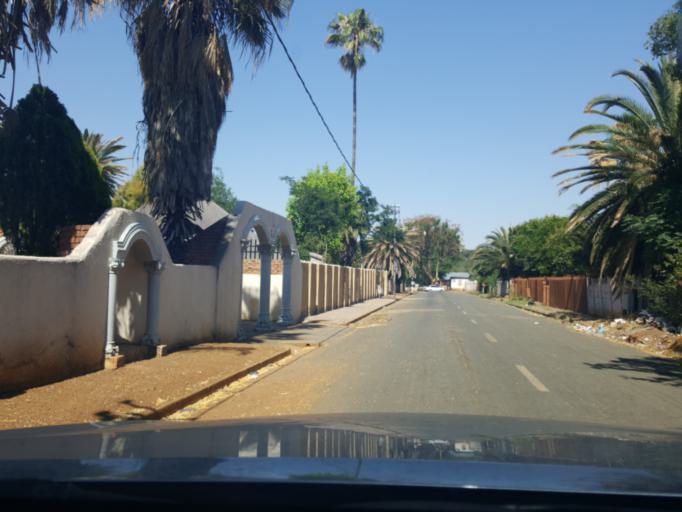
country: ZA
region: North-West
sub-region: Ngaka Modiri Molema District Municipality
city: Zeerust
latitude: -25.5430
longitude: 26.0753
